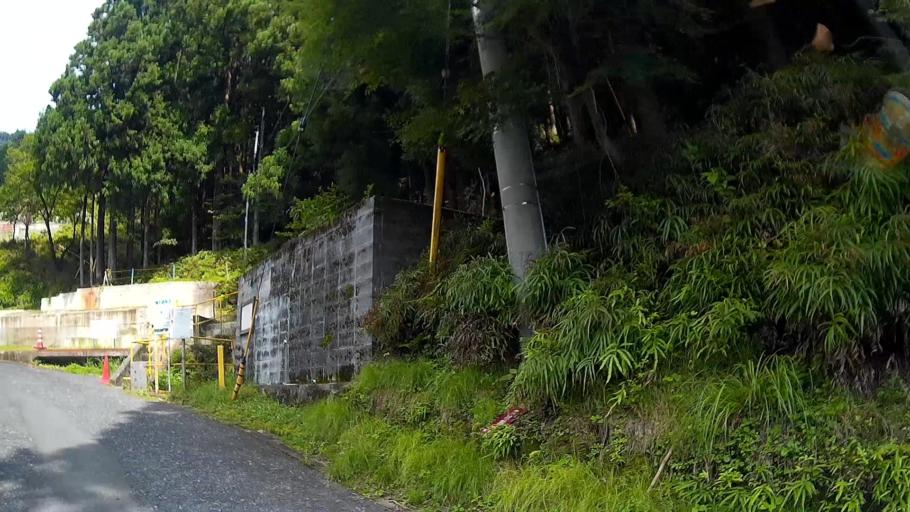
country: JP
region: Saitama
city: Chichibu
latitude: 35.9104
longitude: 139.1268
